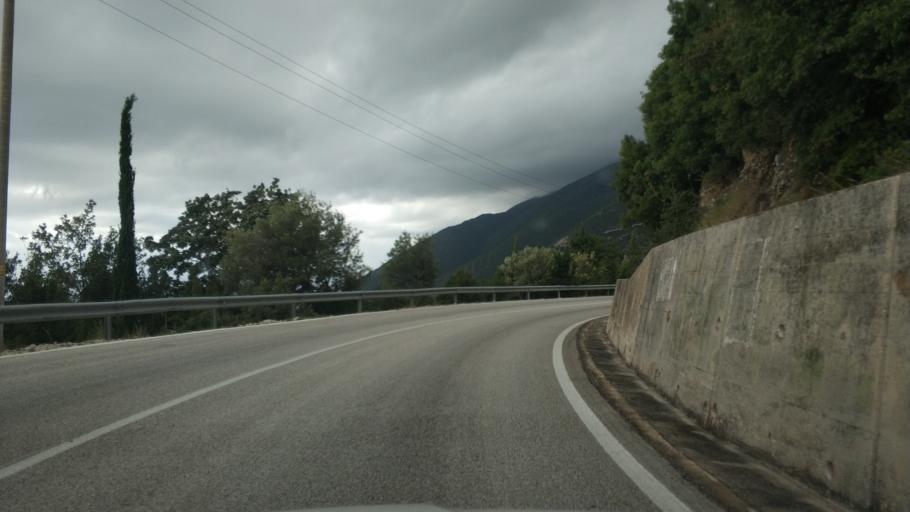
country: AL
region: Vlore
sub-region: Rrethi i Vlores
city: Vranisht
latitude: 40.1702
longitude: 19.6154
